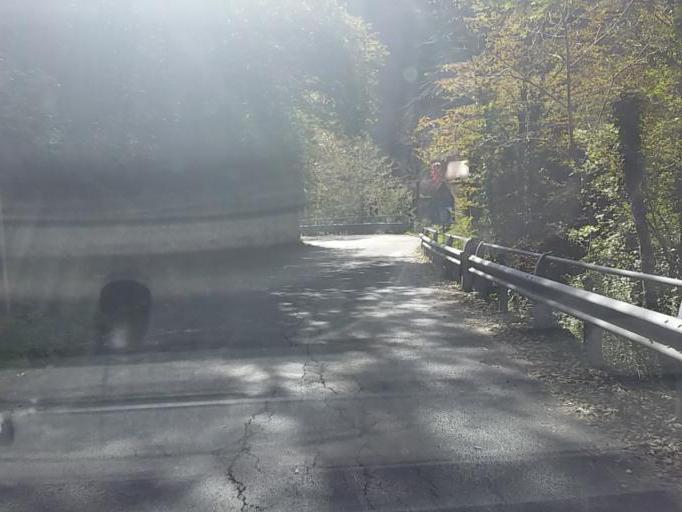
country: IT
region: Piedmont
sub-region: Provincia Verbano-Cusio-Ossola
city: Falmenta
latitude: 46.0903
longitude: 8.5934
